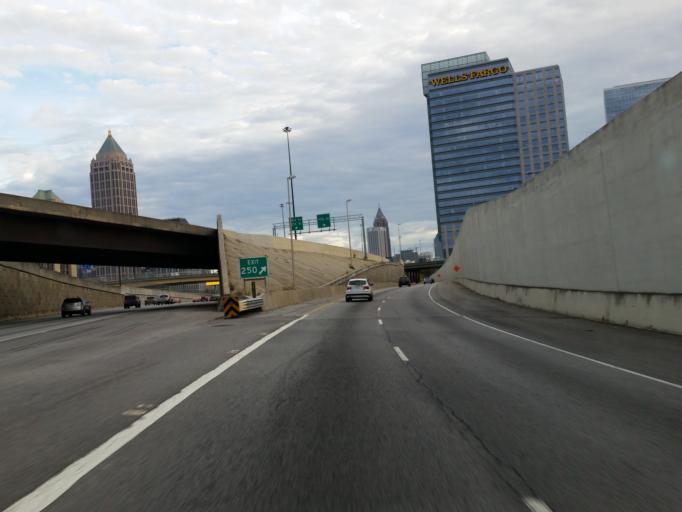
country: US
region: Georgia
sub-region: Fulton County
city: Atlanta
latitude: 33.7951
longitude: -84.3943
